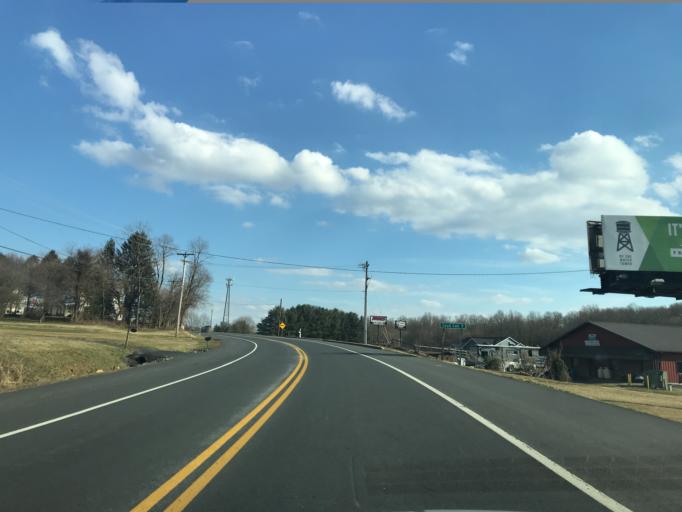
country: US
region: Maryland
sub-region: Cecil County
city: Rising Sun
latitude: 39.6940
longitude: -76.0609
